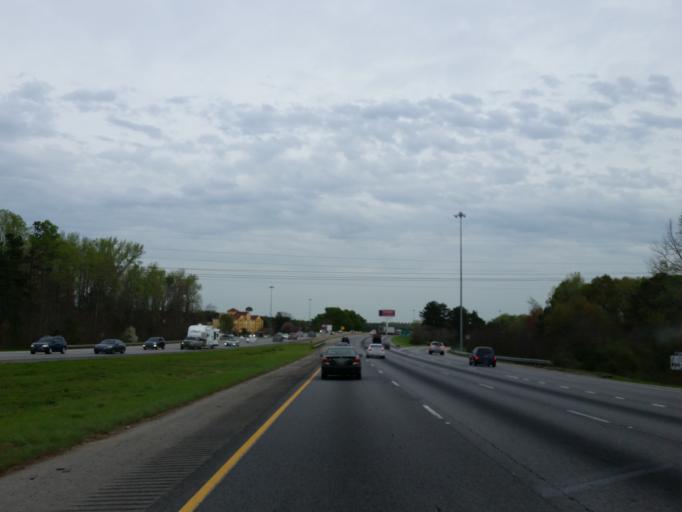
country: US
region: Georgia
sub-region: Henry County
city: Locust Grove
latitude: 33.3567
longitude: -84.1270
